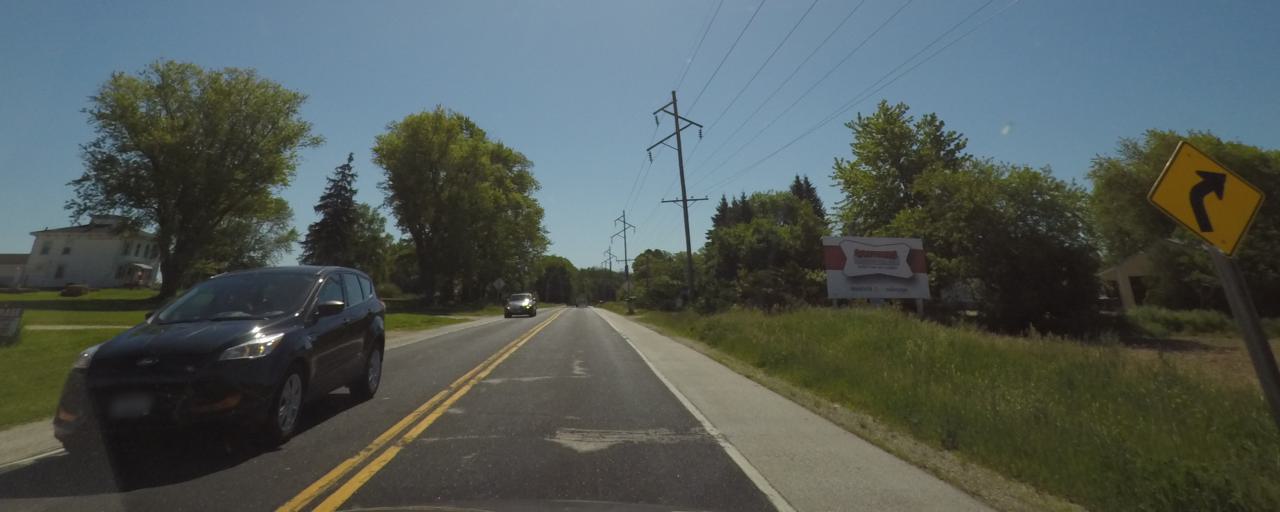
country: US
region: Wisconsin
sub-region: Sheboygan County
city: Sheboygan Falls
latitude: 43.7393
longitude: -87.8493
